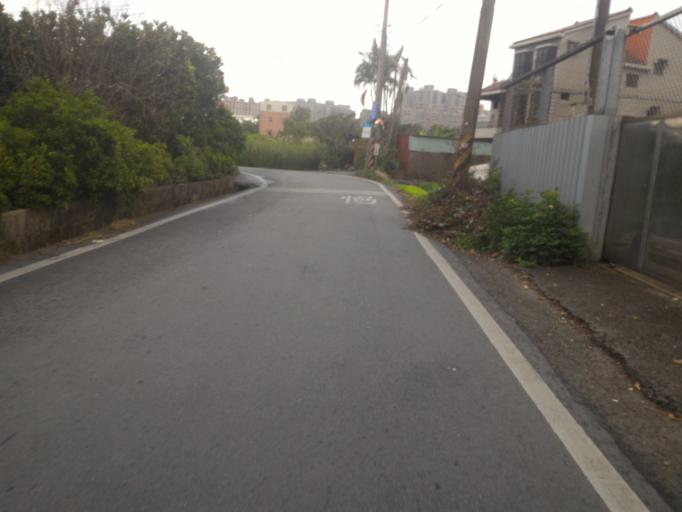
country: TW
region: Taiwan
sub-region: Taoyuan
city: Taoyuan
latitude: 24.9429
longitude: 121.3858
